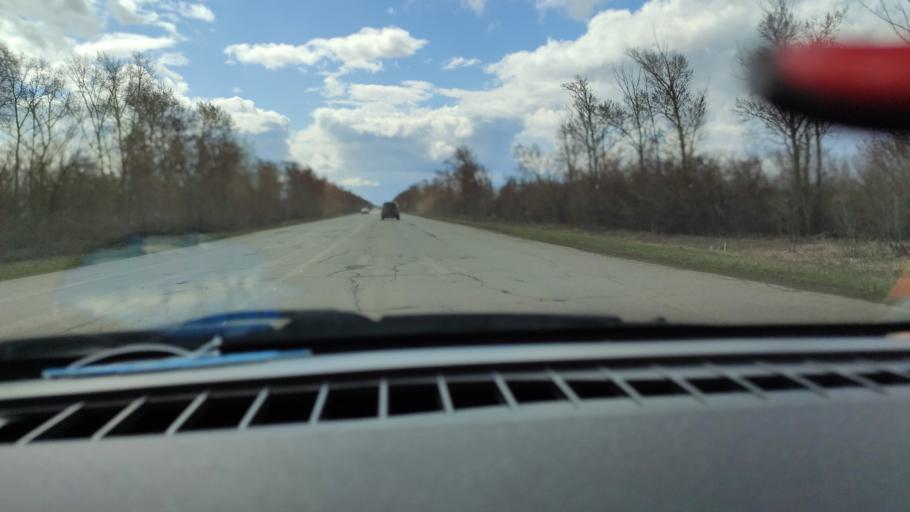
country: RU
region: Samara
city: Tol'yatti
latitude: 53.6030
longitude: 49.4097
